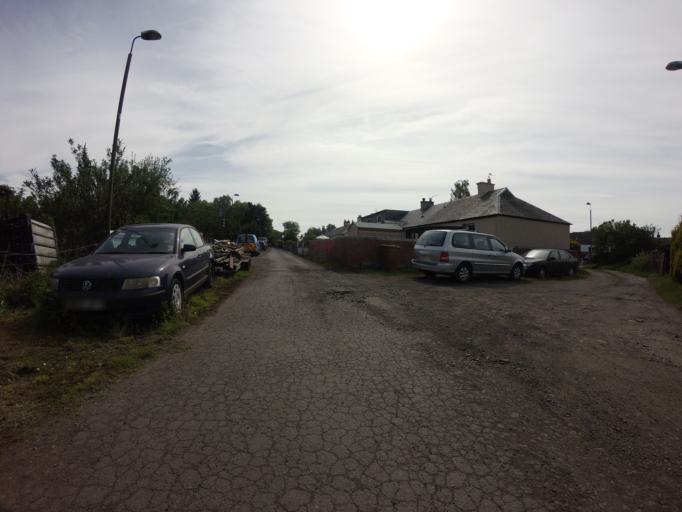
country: GB
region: Scotland
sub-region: West Lothian
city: Broxburn
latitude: 55.9194
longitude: -3.4831
